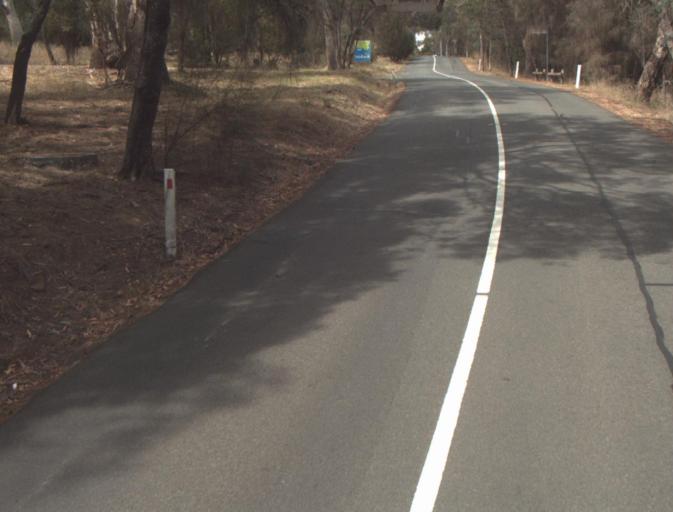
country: AU
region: Tasmania
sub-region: Launceston
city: West Launceston
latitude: -41.4505
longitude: 147.1194
